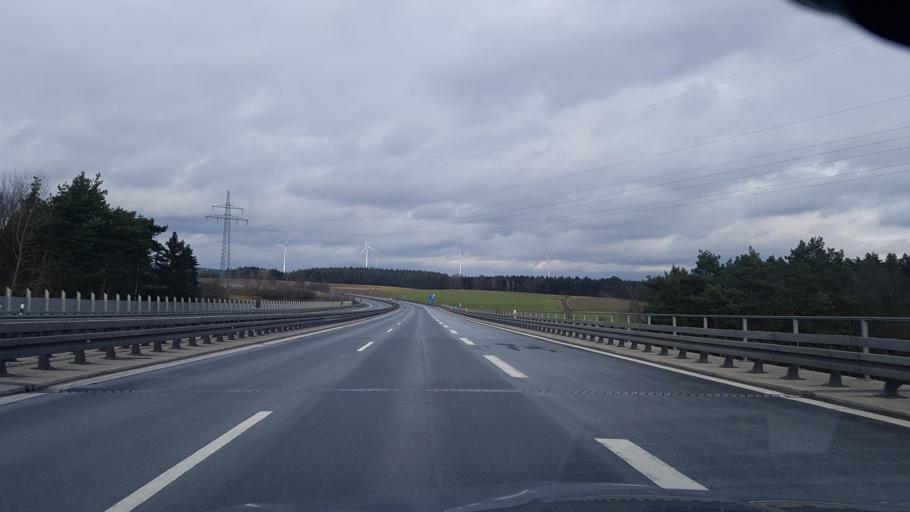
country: DE
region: Bavaria
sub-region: Upper Franconia
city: Marktredwitz
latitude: 50.0196
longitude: 12.1165
